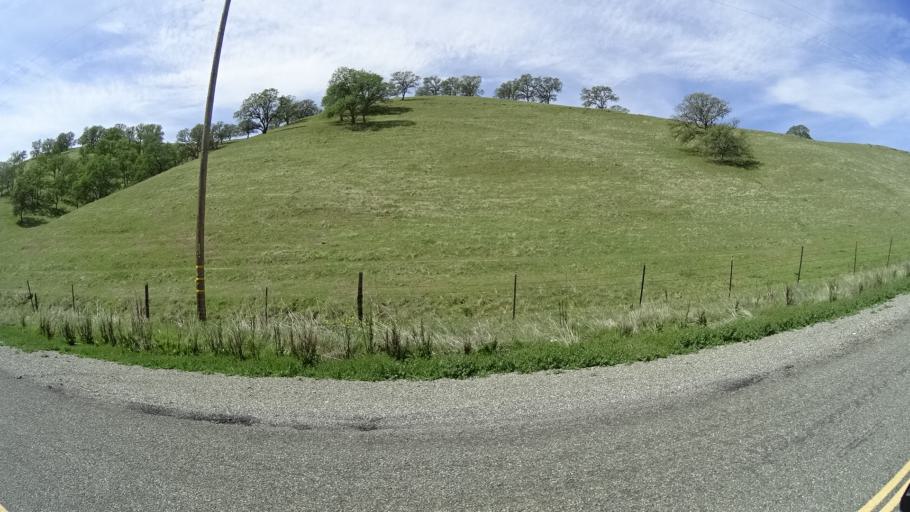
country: US
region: California
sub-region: Glenn County
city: Willows
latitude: 39.5707
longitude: -122.4432
